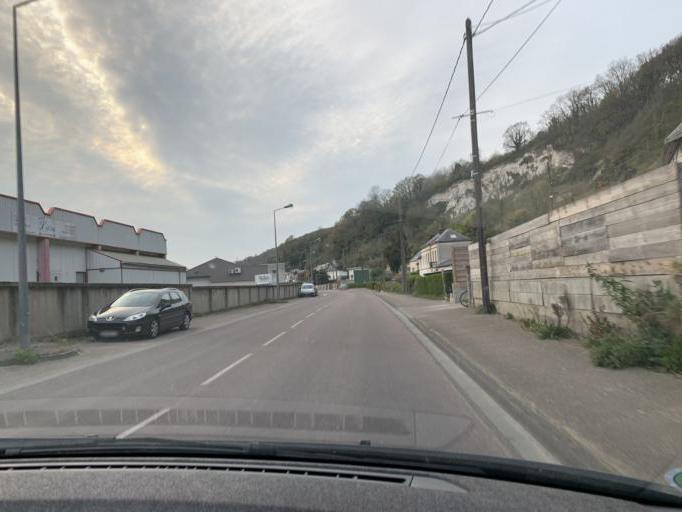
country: FR
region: Haute-Normandie
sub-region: Departement de la Seine-Maritime
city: Fecamp
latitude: 49.7558
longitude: 0.4017
